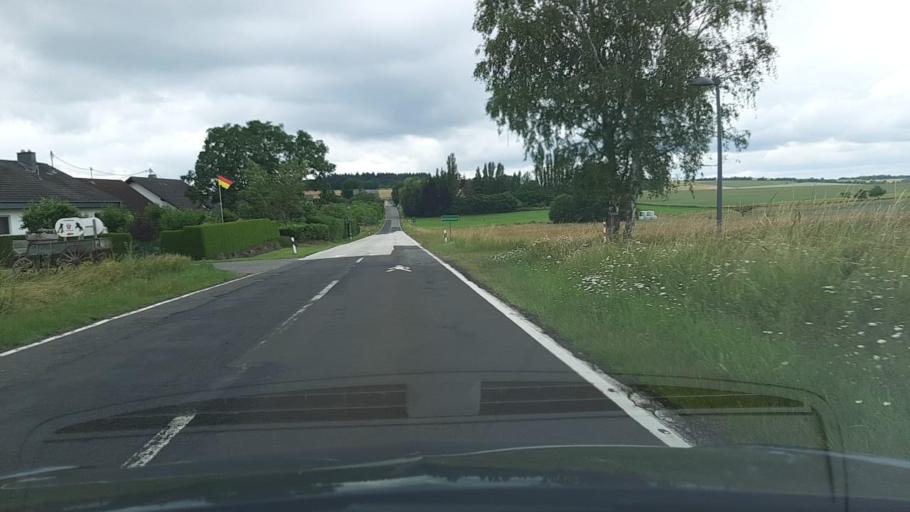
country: DE
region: Rheinland-Pfalz
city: Dommershausen
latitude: 50.1440
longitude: 7.4050
